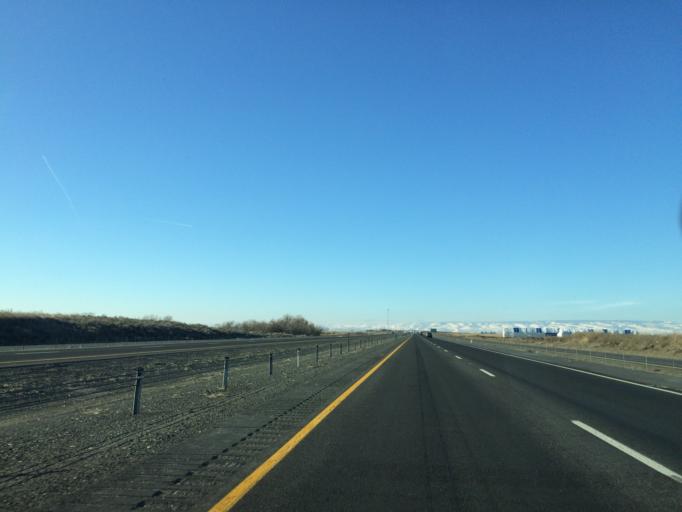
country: US
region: Washington
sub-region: Grant County
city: Quincy
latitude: 47.1036
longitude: -119.7416
